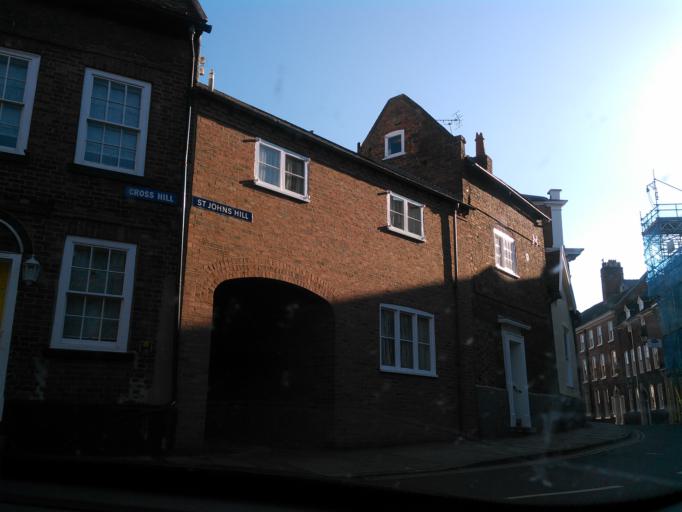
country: GB
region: England
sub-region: Shropshire
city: Shrewsbury
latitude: 52.7070
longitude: -2.7572
